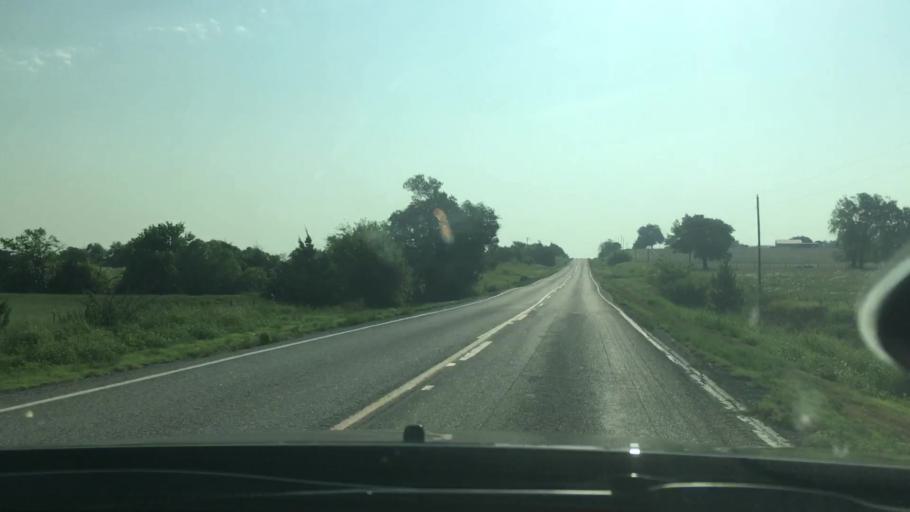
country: US
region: Oklahoma
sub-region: Bryan County
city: Durant
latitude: 34.1427
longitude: -96.3188
